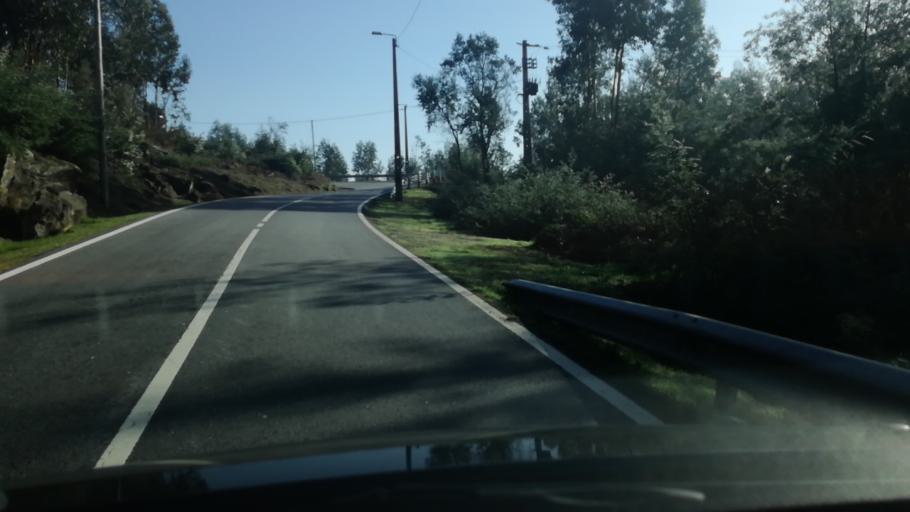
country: PT
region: Braga
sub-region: Guimaraes
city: Ponte
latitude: 41.5260
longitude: -8.3183
